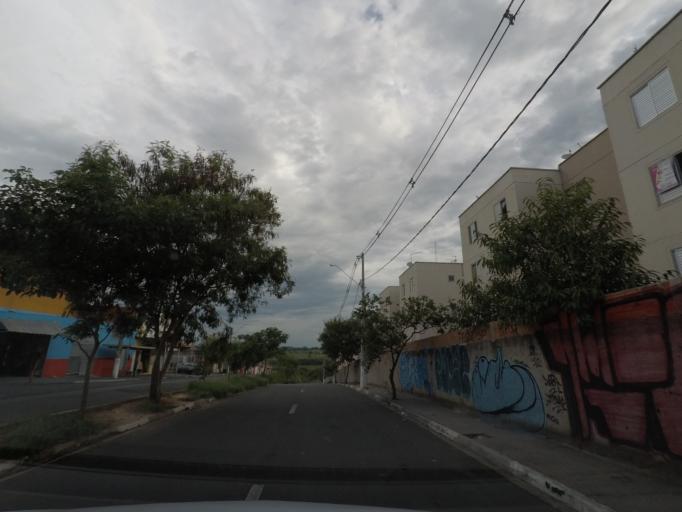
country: BR
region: Sao Paulo
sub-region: Hortolandia
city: Hortolandia
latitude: -22.9646
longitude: -47.2010
